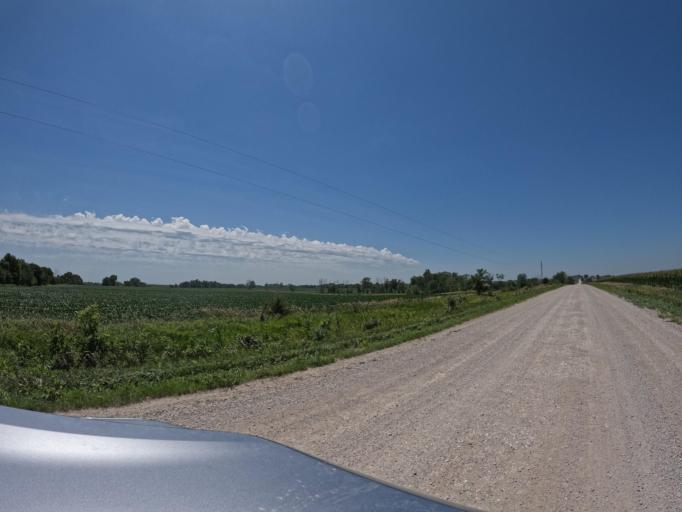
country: US
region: Iowa
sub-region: Keokuk County
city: Sigourney
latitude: 41.4090
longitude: -92.3215
